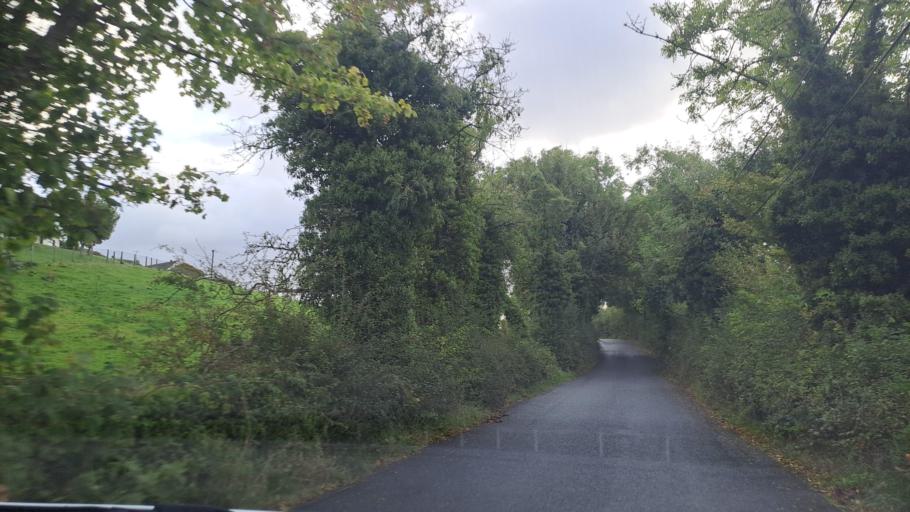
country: IE
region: Ulster
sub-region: An Cabhan
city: Kingscourt
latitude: 53.9563
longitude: -6.7926
